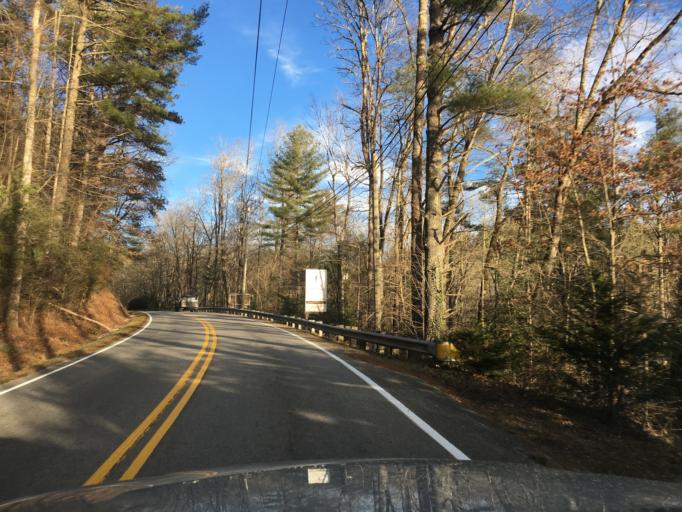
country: US
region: North Carolina
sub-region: Transylvania County
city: Brevard
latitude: 35.1101
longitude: -82.9691
